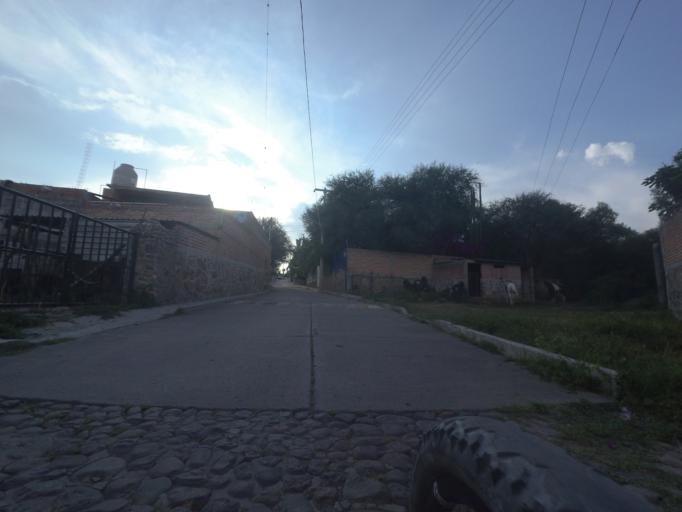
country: MX
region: Aguascalientes
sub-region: Aguascalientes
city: Los Canos
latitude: 21.7800
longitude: -102.3740
